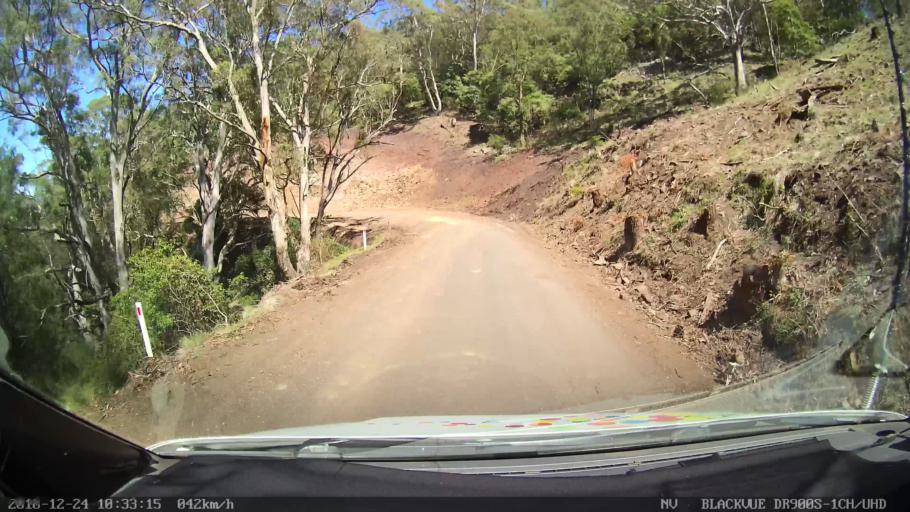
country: AU
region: New South Wales
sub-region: Upper Hunter Shire
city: Merriwa
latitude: -31.8411
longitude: 150.5114
